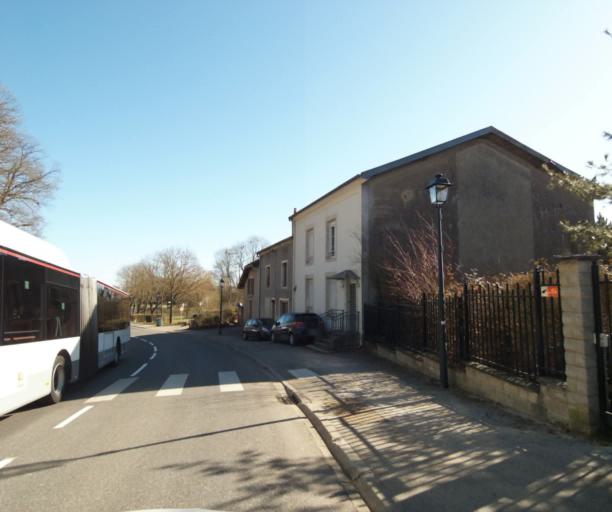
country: FR
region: Lorraine
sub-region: Departement de Meurthe-et-Moselle
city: Ludres
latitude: 48.6204
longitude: 6.1649
